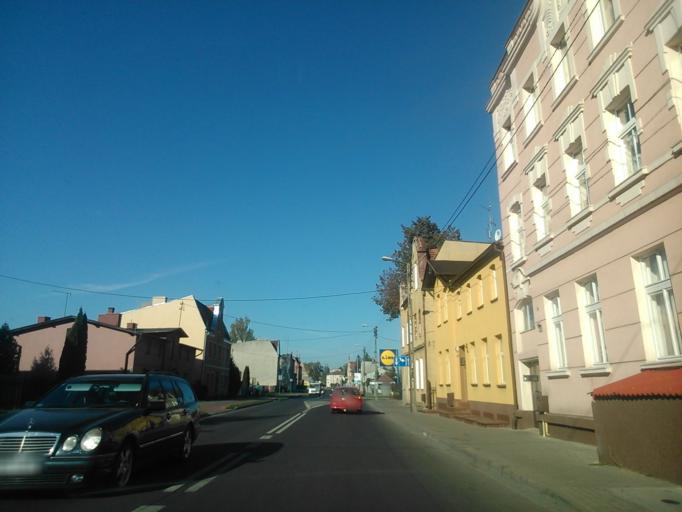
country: PL
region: Kujawsko-Pomorskie
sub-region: Powiat wabrzeski
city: Wabrzezno
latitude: 53.2787
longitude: 18.9616
